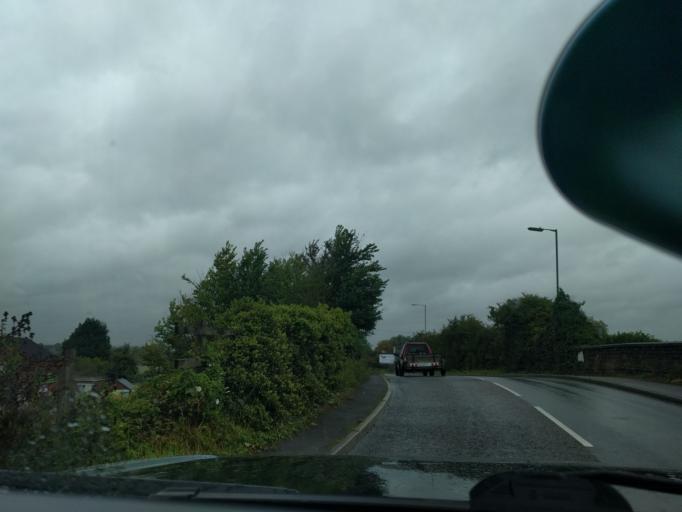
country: GB
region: England
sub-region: Wiltshire
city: Melksham
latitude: 51.3793
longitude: -2.1446
